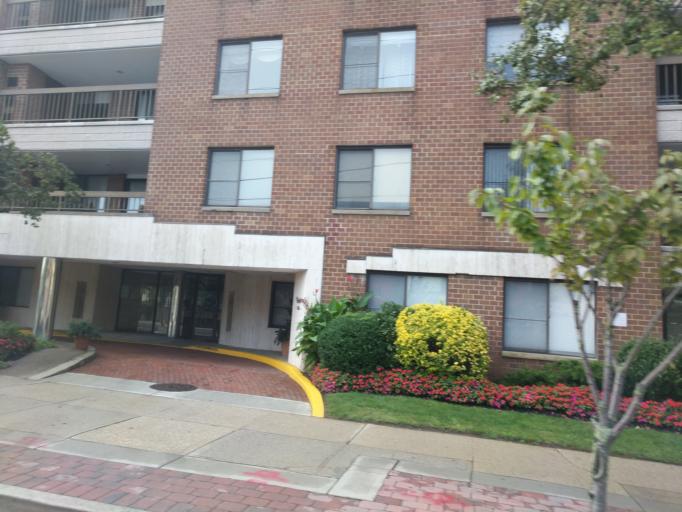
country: US
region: New York
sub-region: Nassau County
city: Lawrence
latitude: 40.6191
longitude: -73.7273
